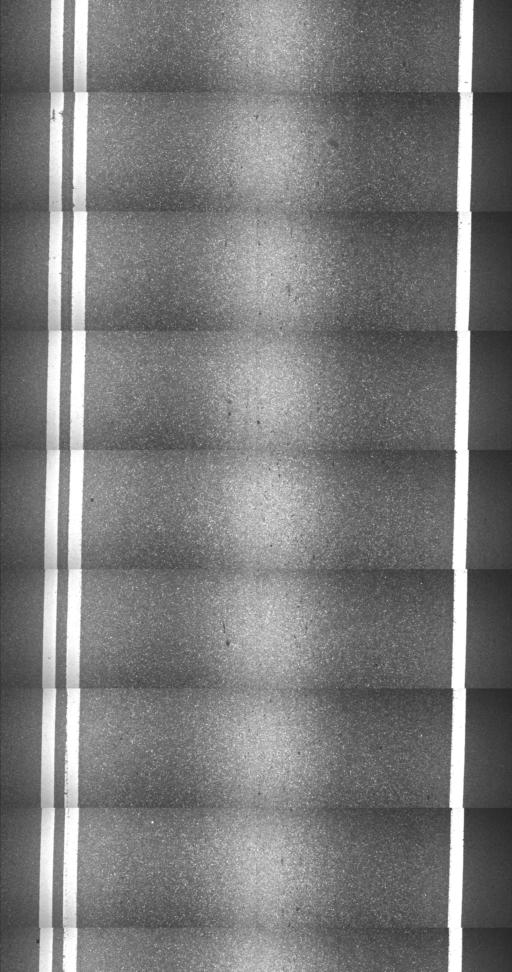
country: US
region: Vermont
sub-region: Washington County
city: Waterbury
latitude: 44.2390
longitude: -72.7755
